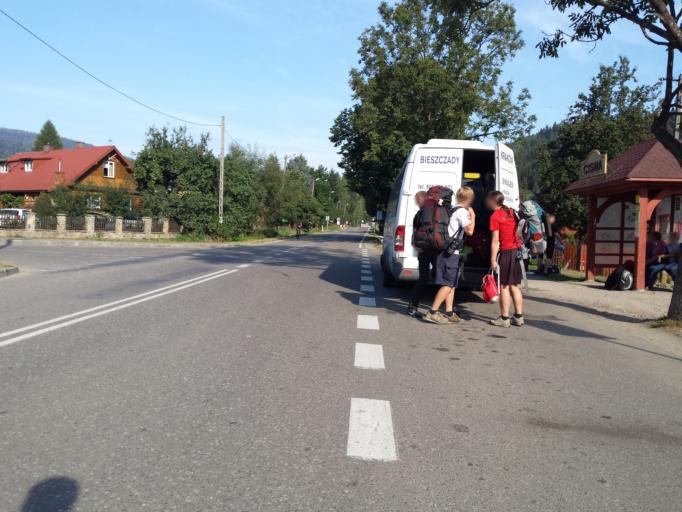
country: PL
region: Subcarpathian Voivodeship
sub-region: Powiat leski
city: Cisna
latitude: 49.2133
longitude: 22.3280
